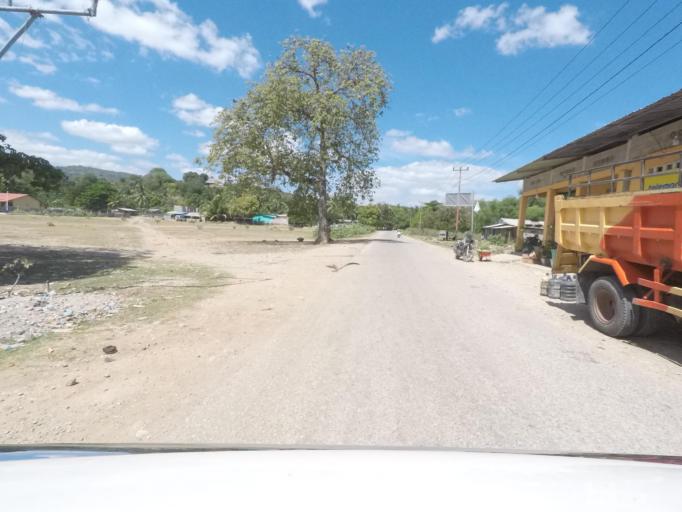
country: TL
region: Lautem
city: Lospalos
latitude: -8.3643
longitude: 126.9018
